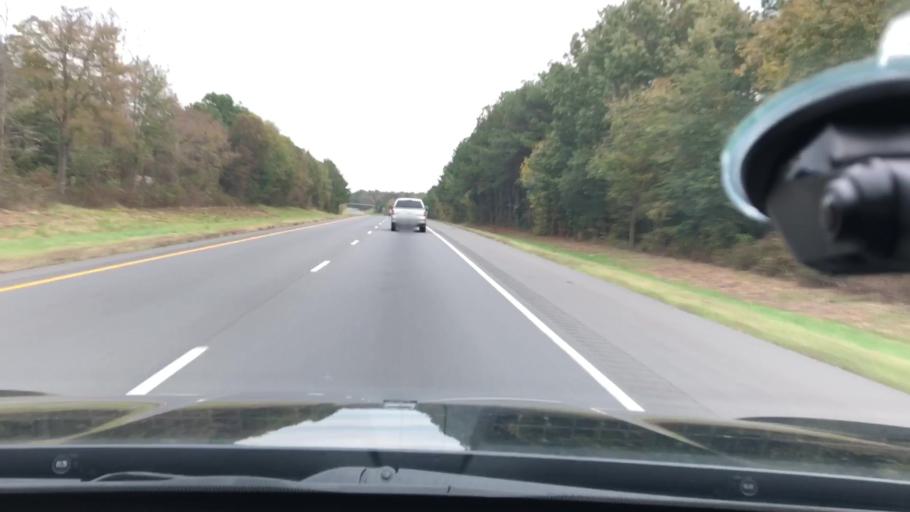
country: US
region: Arkansas
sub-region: Hempstead County
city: Hope
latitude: 33.7326
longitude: -93.5308
